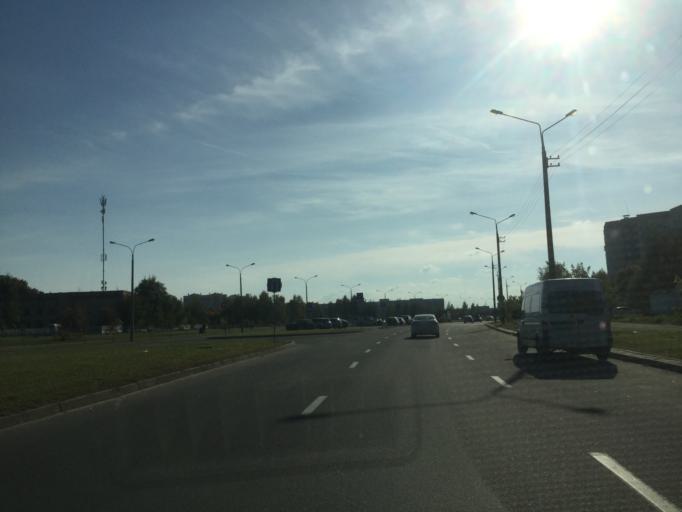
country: BY
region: Vitebsk
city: Vitebsk
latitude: 55.1607
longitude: 30.2206
